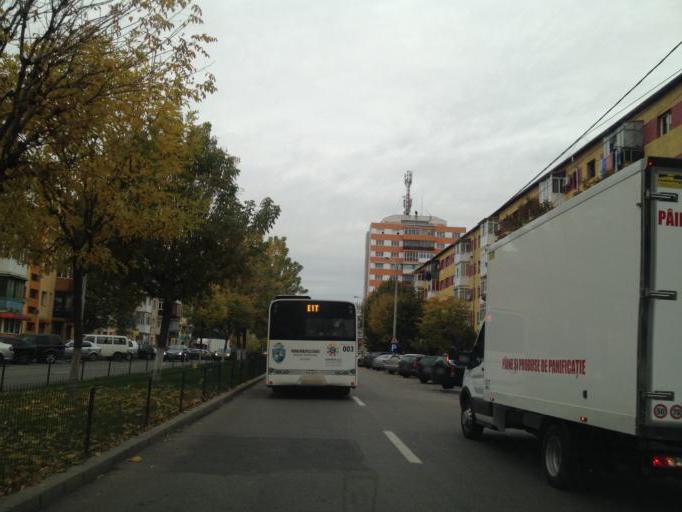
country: RO
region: Dolj
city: Craiova
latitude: 44.3367
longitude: 23.7834
